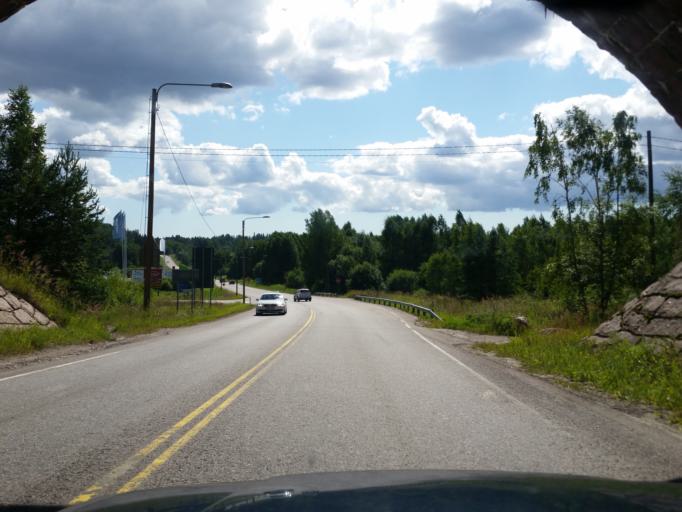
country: FI
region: Uusimaa
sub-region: Helsinki
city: Vihti
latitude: 60.3109
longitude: 24.2427
